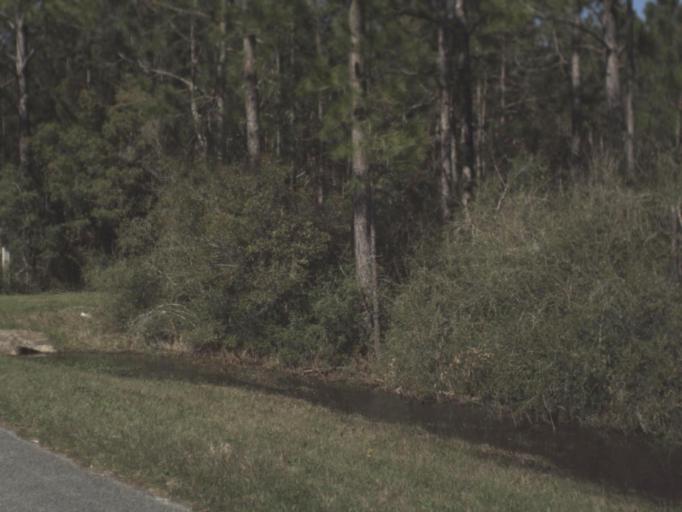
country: US
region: Florida
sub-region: Gulf County
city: Wewahitchka
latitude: 30.0041
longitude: -85.1736
